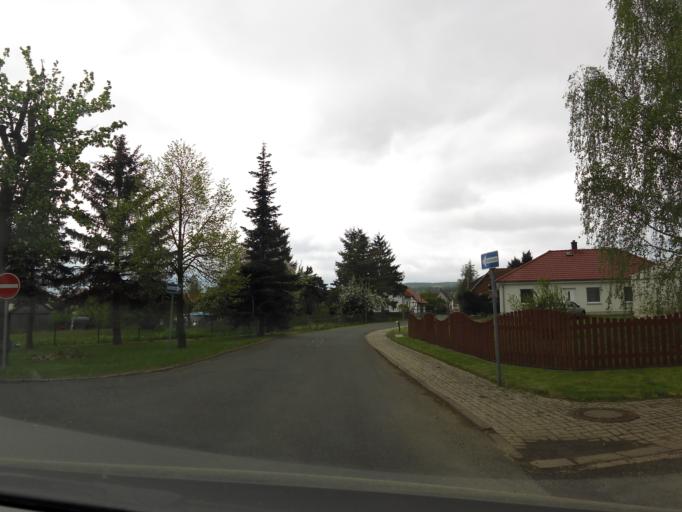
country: DE
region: Thuringia
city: Ernstroda
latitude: 50.8825
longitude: 10.6144
